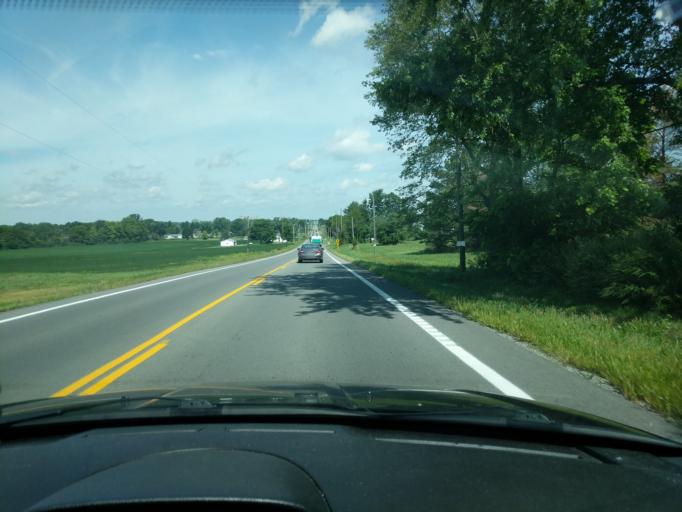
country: US
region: Ohio
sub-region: Logan County
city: Bellefontaine
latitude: 40.3108
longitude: -83.7599
